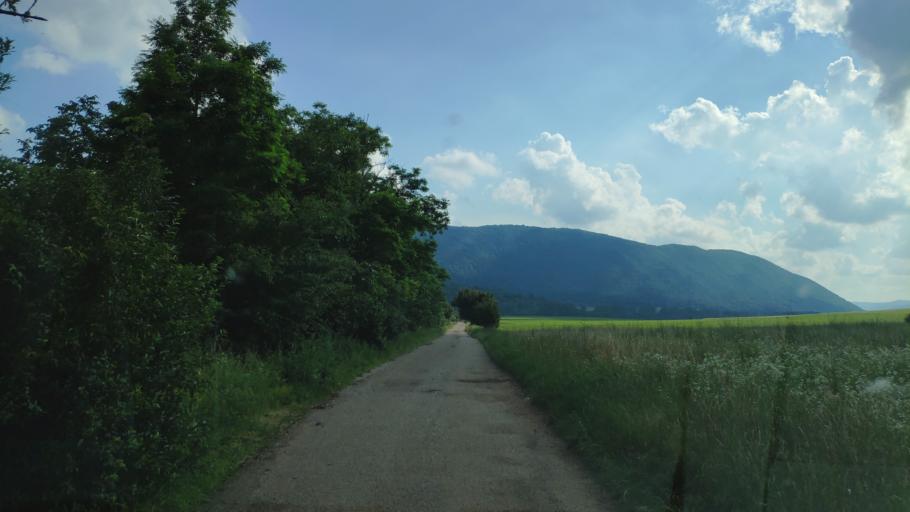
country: SK
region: Kosicky
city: Medzev
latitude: 48.5987
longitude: 20.7352
